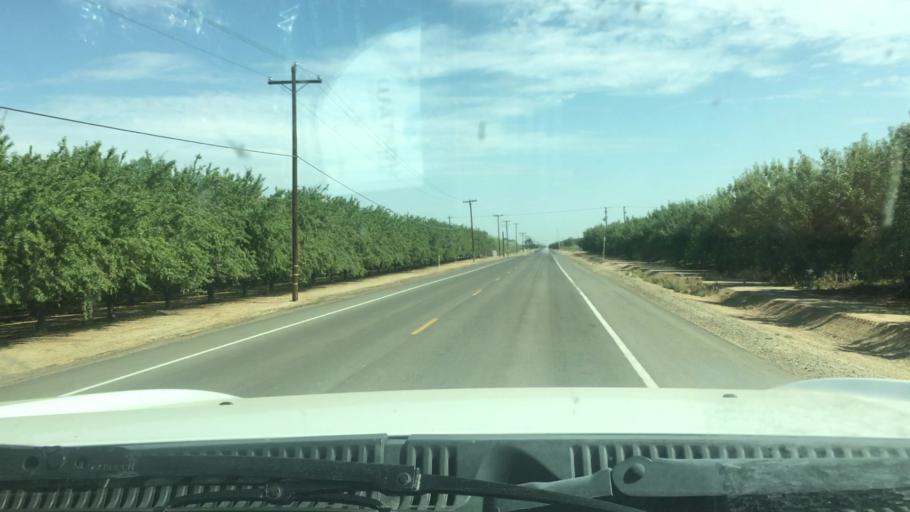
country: US
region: California
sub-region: Kern County
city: Wasco
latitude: 35.5557
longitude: -119.4742
